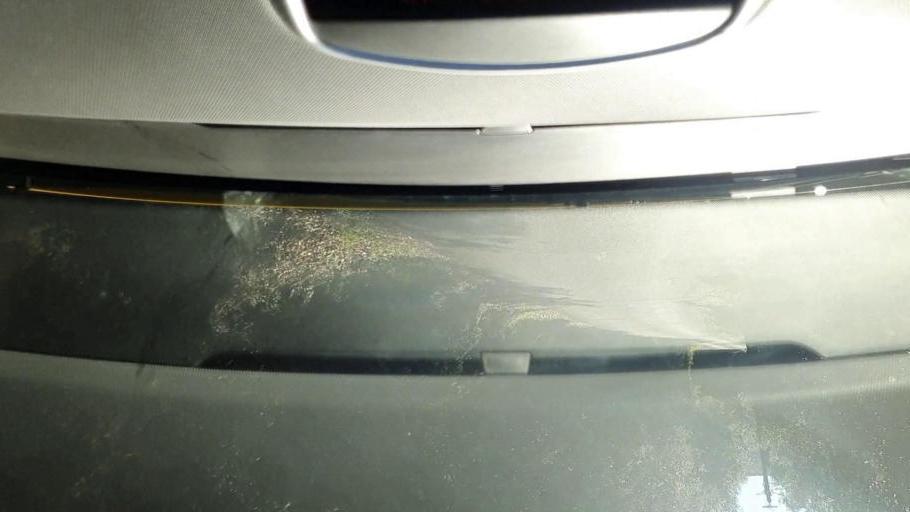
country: FR
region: Languedoc-Roussillon
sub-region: Departement du Gard
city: Sumene
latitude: 44.0514
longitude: 3.7112
